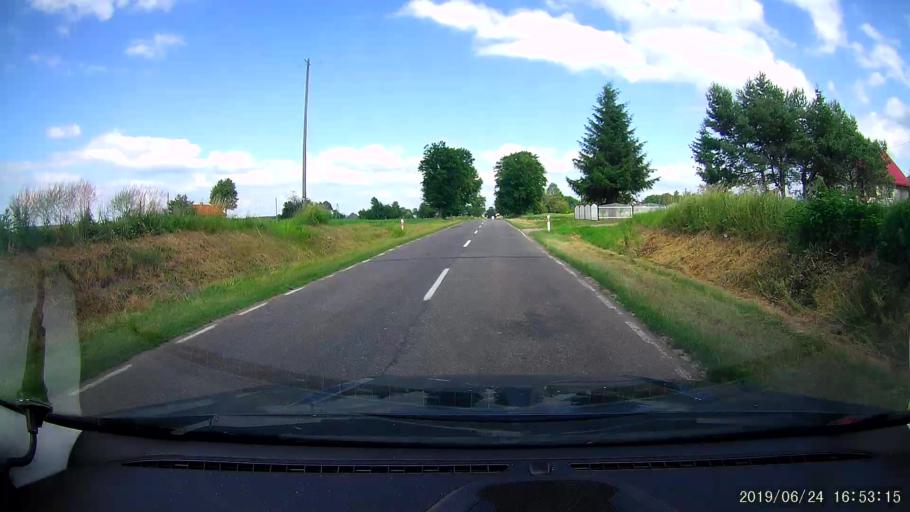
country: PL
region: Lublin Voivodeship
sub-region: Powiat tomaszowski
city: Telatyn
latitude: 50.5355
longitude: 23.7971
